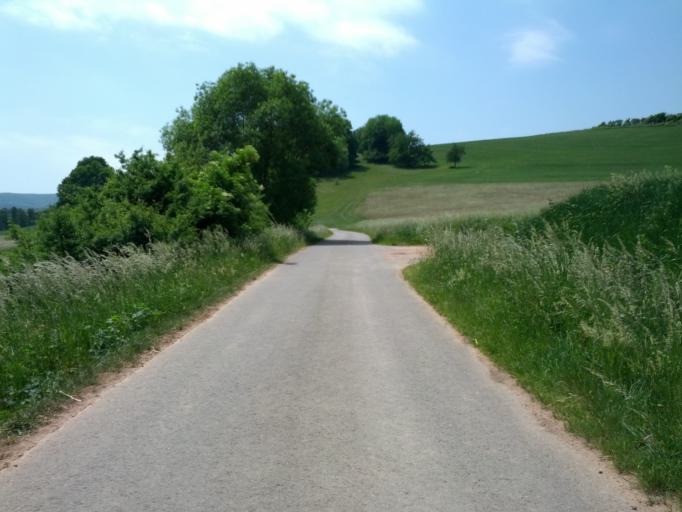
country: DE
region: Thuringia
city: Urnshausen
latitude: 50.7281
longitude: 10.1661
